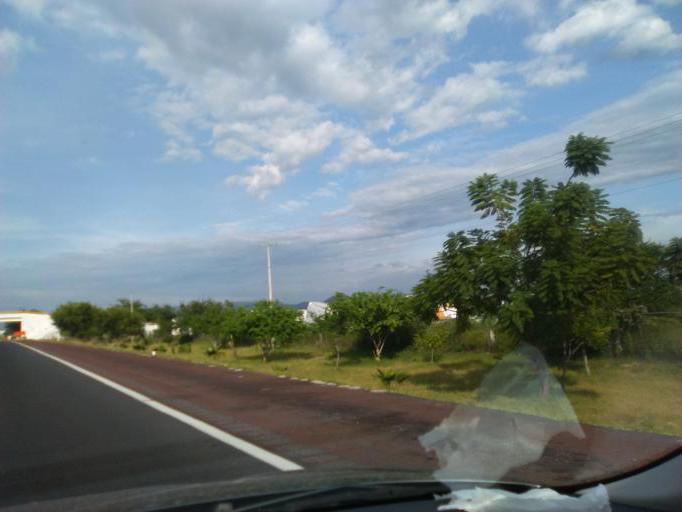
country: MX
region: Morelos
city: Xoxocotla
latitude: 18.7017
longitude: -99.2759
